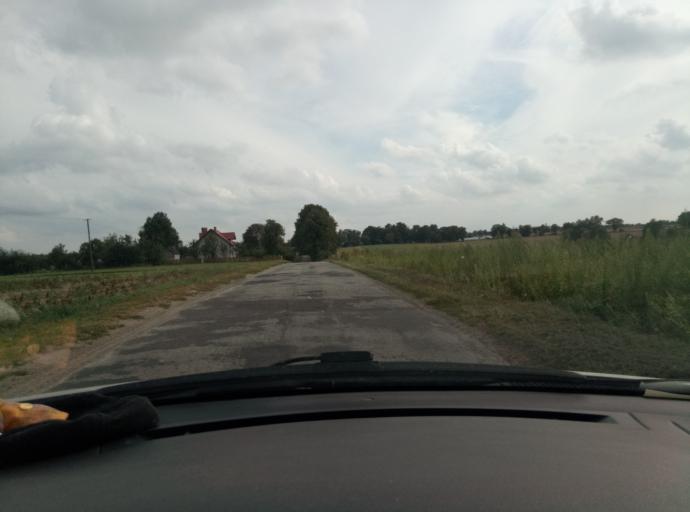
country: PL
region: Kujawsko-Pomorskie
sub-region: Powiat brodnicki
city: Jablonowo Pomorskie
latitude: 53.3791
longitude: 19.2451
